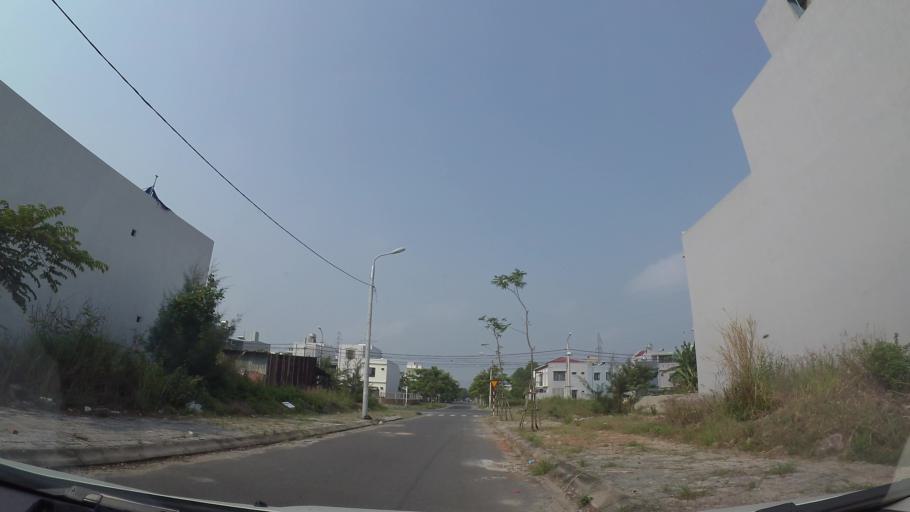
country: VN
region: Da Nang
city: Ngu Hanh Son
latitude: 16.0271
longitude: 108.2437
